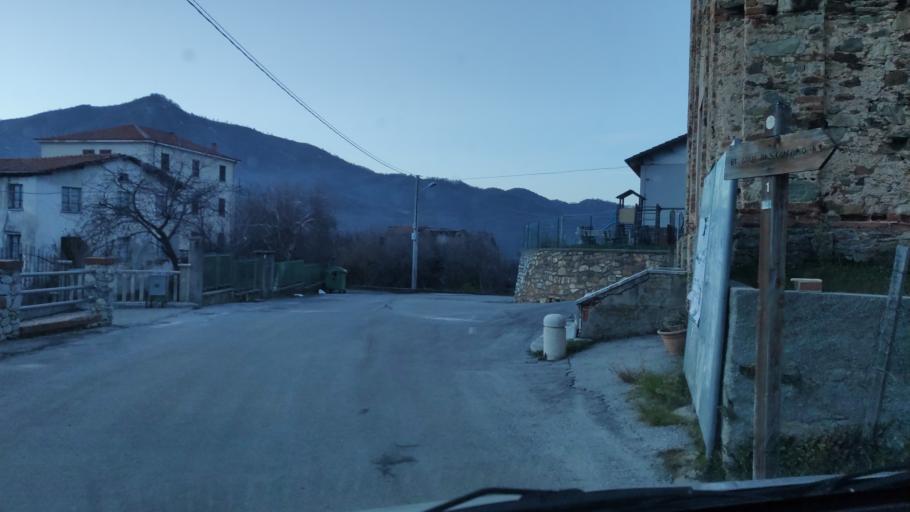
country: IT
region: Piedmont
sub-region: Provincia di Cuneo
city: Viola
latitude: 44.2875
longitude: 7.9841
